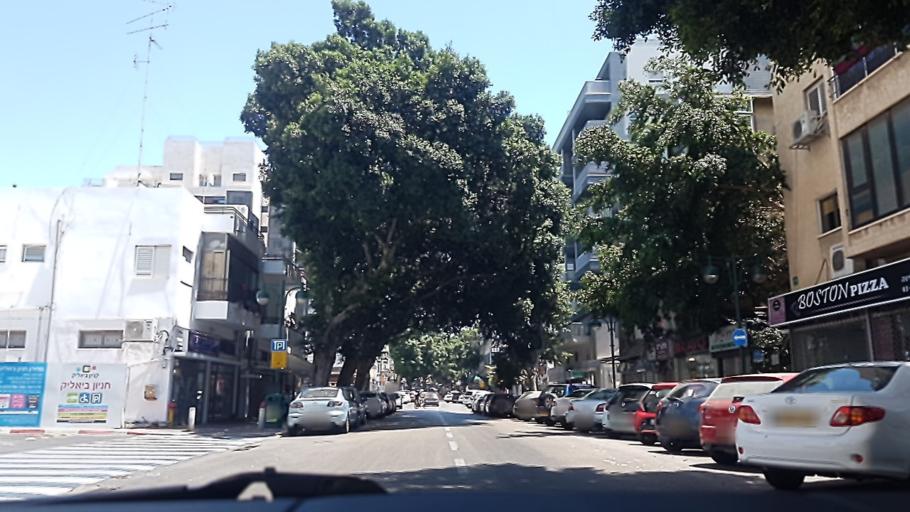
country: IL
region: Tel Aviv
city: Ramat Gan
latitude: 32.0854
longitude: 34.8114
